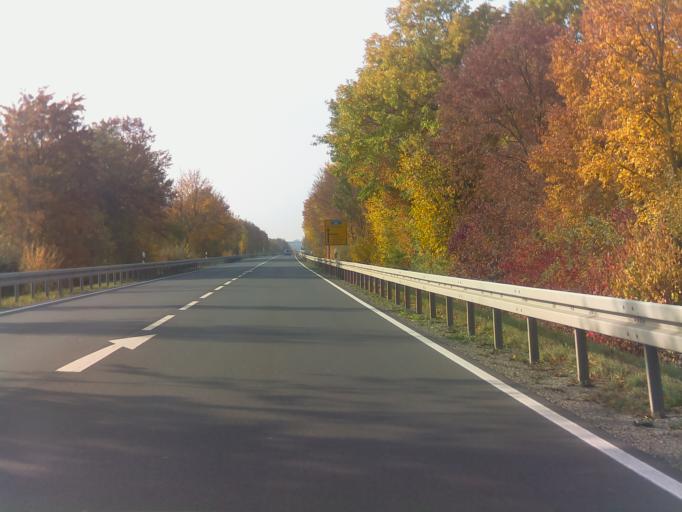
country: DE
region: Bavaria
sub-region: Regierungsbezirk Unterfranken
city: Biebelried
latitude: 49.7883
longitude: 10.0998
